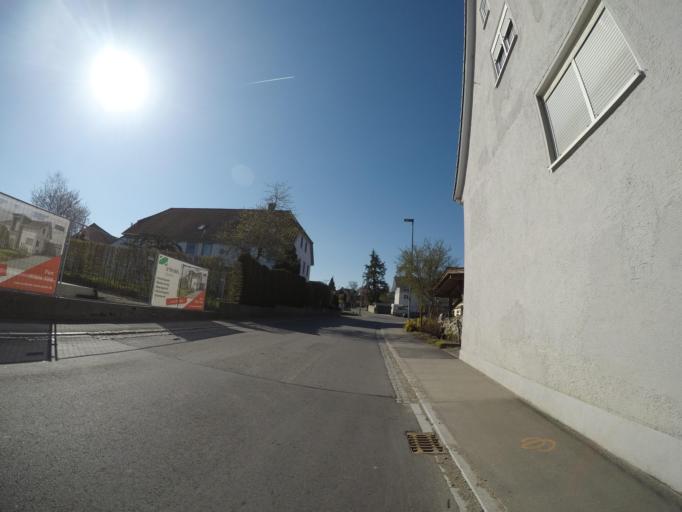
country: DE
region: Baden-Wuerttemberg
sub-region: Tuebingen Region
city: Ebenweiler
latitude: 47.8995
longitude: 9.5135
